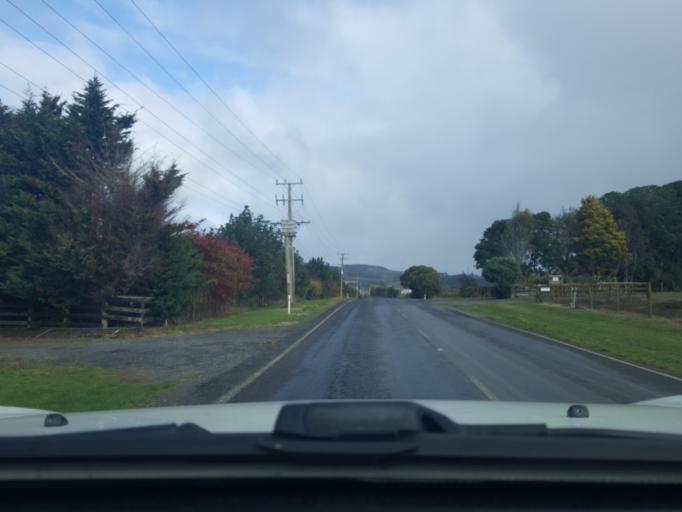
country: NZ
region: Auckland
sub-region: Auckland
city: Pukekohe East
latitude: -37.3017
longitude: 175.0206
